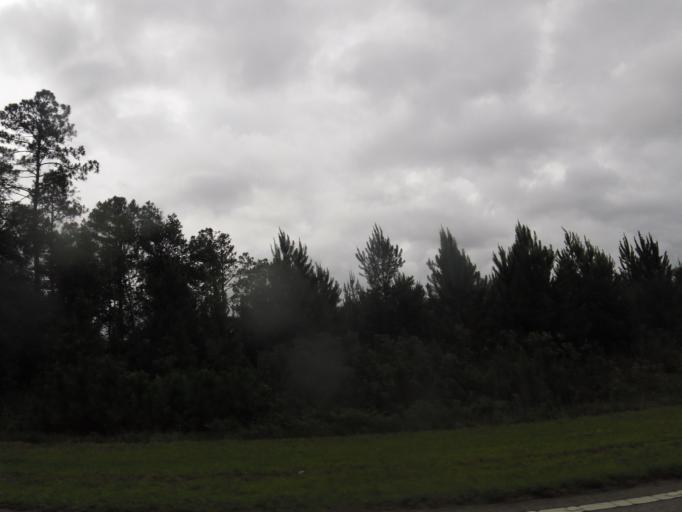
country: US
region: Florida
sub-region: Saint Johns County
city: Saint Augustine South
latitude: 29.8531
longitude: -81.4772
